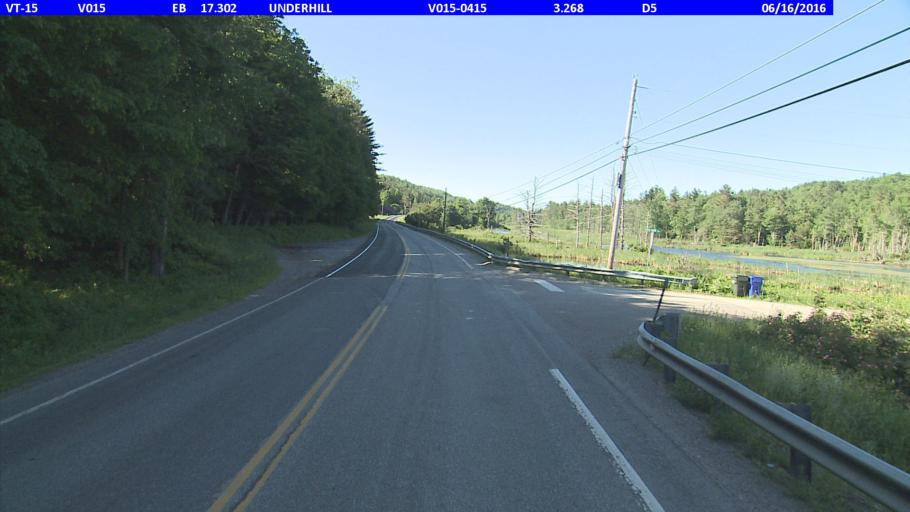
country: US
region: Vermont
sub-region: Chittenden County
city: Jericho
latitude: 44.5707
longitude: -72.9414
